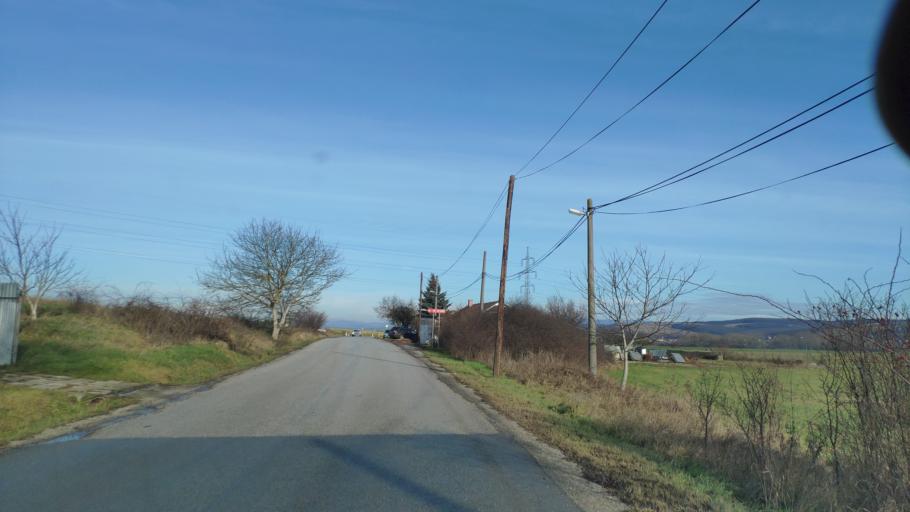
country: SK
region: Kosicky
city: Kosice
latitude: 48.6755
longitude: 21.3232
